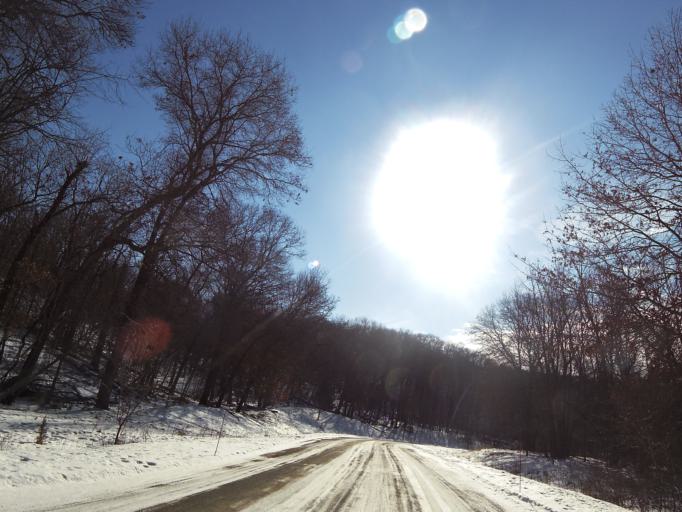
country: US
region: Wisconsin
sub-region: Saint Croix County
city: North Hudson
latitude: 45.0116
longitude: -92.6995
